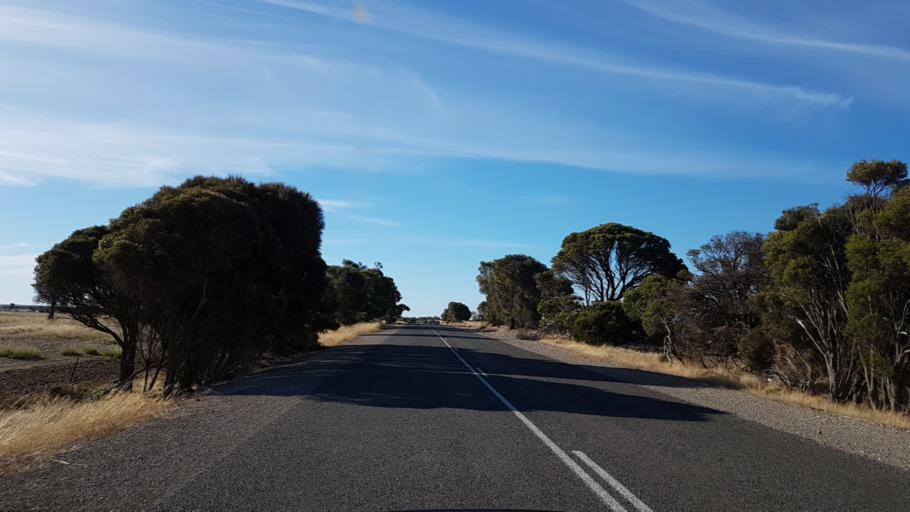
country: AU
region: South Australia
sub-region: Yorke Peninsula
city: Honiton
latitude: -34.9458
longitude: 137.0960
